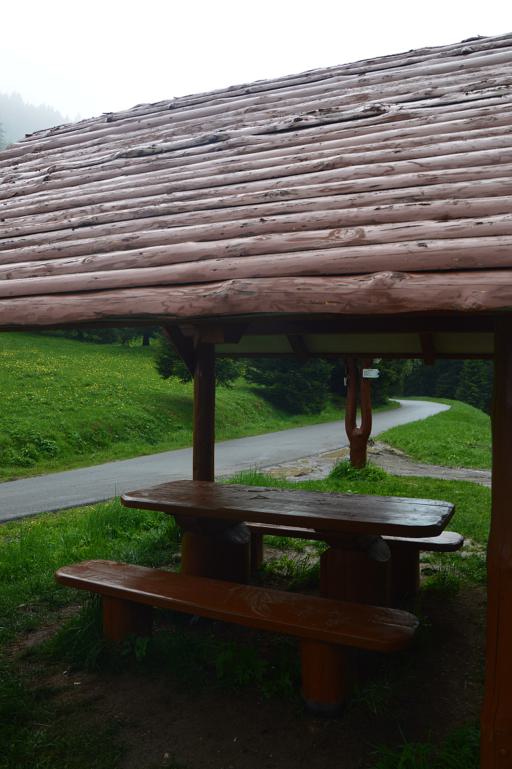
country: SK
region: Kosicky
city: Dobsina
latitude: 48.9003
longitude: 20.2948
